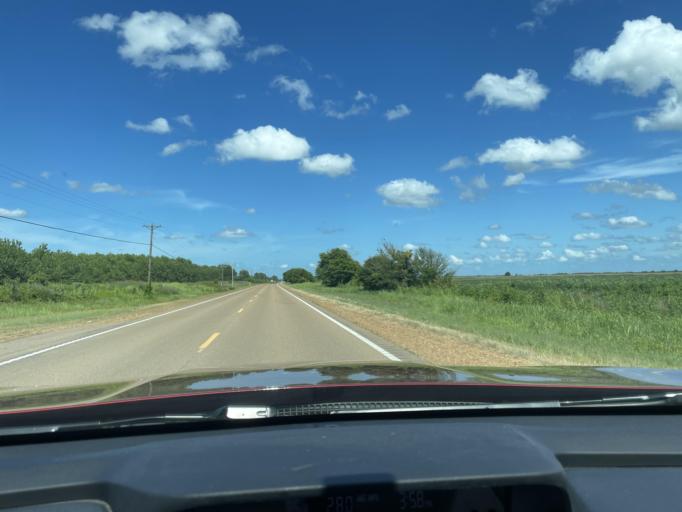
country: US
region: Mississippi
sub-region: Humphreys County
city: Belzoni
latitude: 33.1836
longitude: -90.5944
